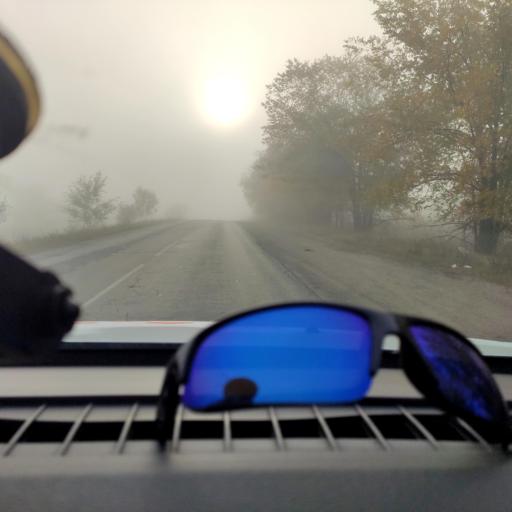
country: RU
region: Samara
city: Chapayevsk
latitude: 53.0054
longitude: 49.7439
